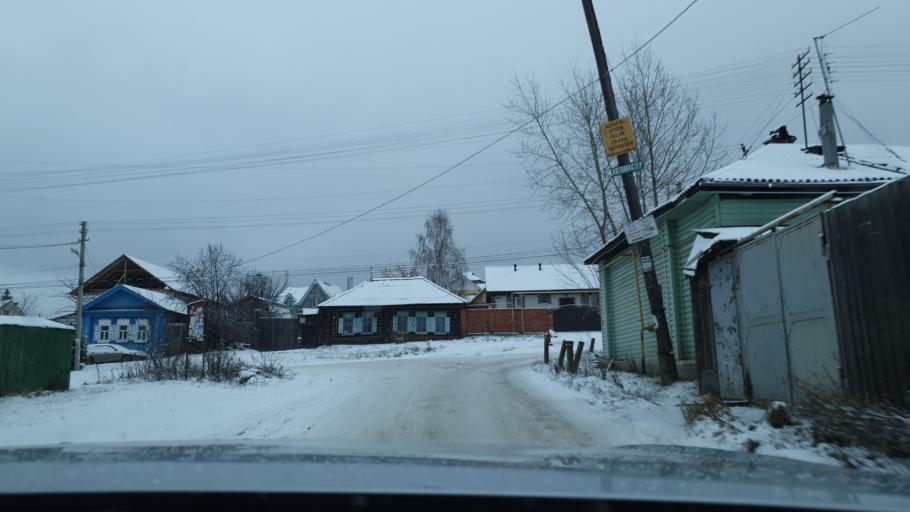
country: RU
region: Sverdlovsk
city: Istok
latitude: 56.7478
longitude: 60.6998
